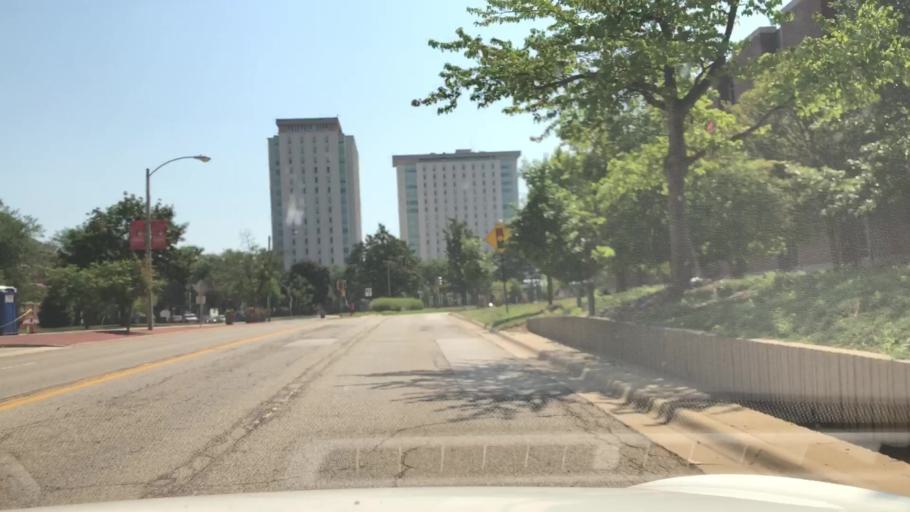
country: US
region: Illinois
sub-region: McLean County
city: Normal
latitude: 40.5108
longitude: -88.9908
